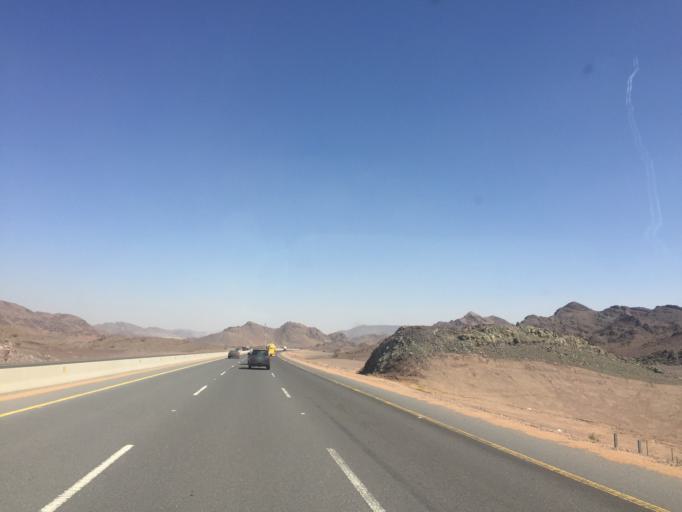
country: SA
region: Al Madinah al Munawwarah
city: Sultanah
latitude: 24.3118
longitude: 39.4158
